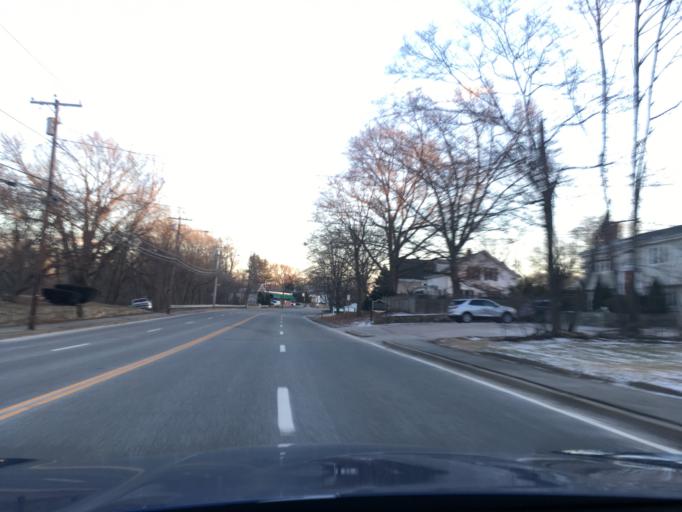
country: US
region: Rhode Island
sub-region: Kent County
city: East Greenwich
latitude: 41.7046
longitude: -71.4625
